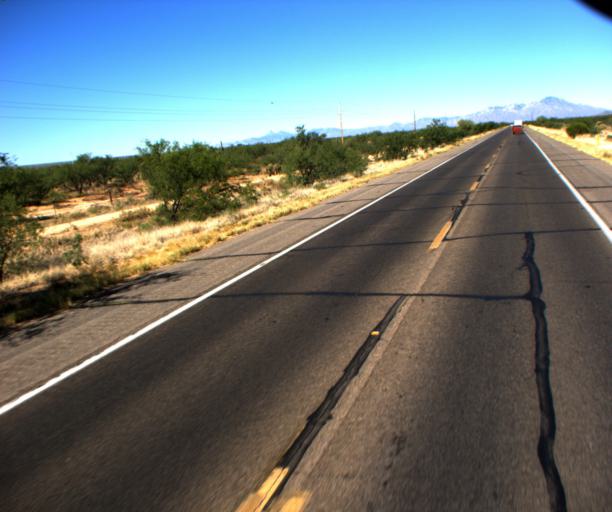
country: US
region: Arizona
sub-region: Pima County
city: Three Points
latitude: 32.1090
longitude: -111.2325
